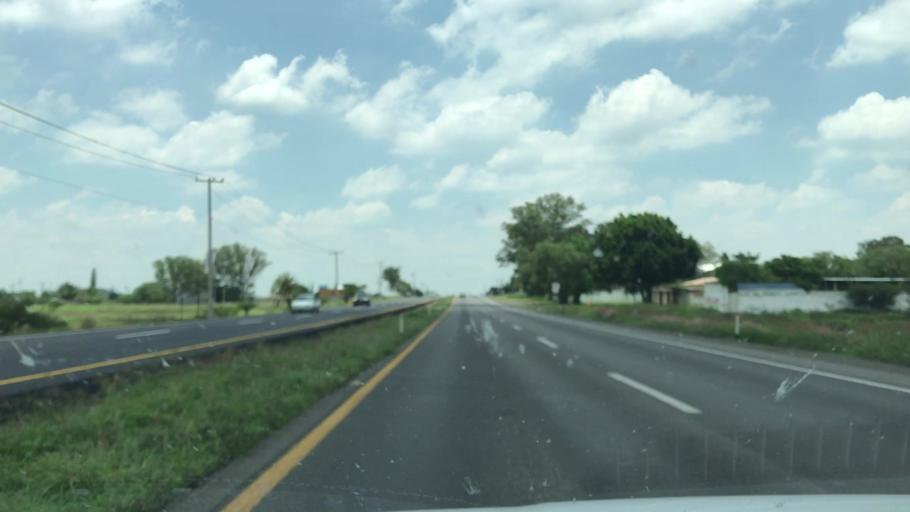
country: MX
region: Guanajuato
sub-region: Irapuato
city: San Ignacio de Rivera (Ojo de Agua)
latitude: 20.5398
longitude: -101.4569
